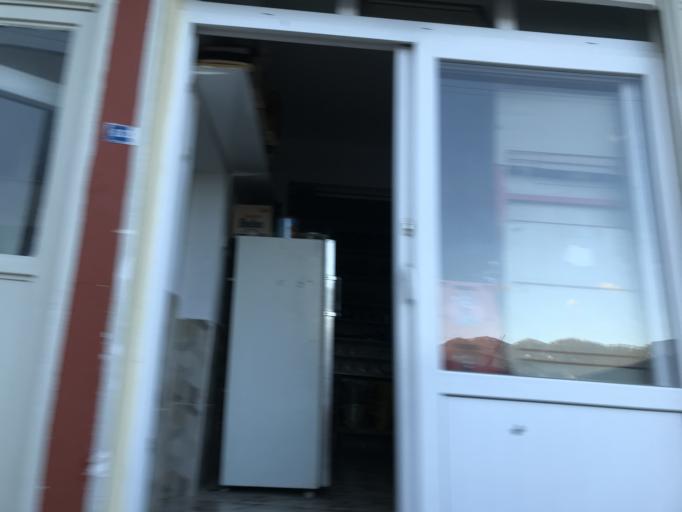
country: TR
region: Hatay
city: Buyukcat
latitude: 36.1000
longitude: 36.0580
